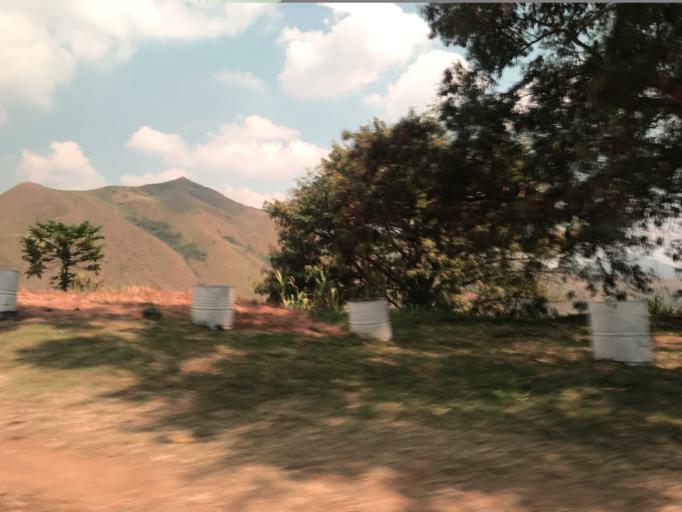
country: CO
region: Valle del Cauca
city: Cali
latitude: 3.4609
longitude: -76.5853
